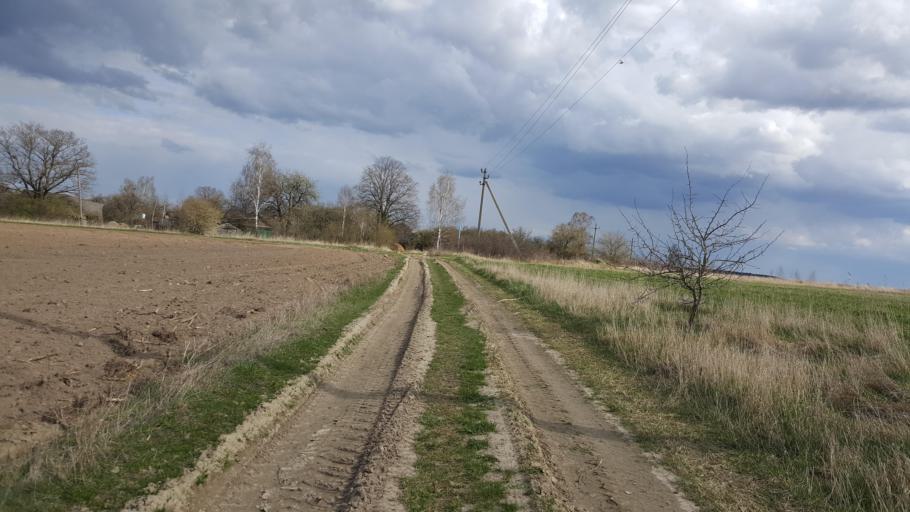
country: BY
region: Brest
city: Kamyanyets
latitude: 52.4383
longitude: 23.6790
